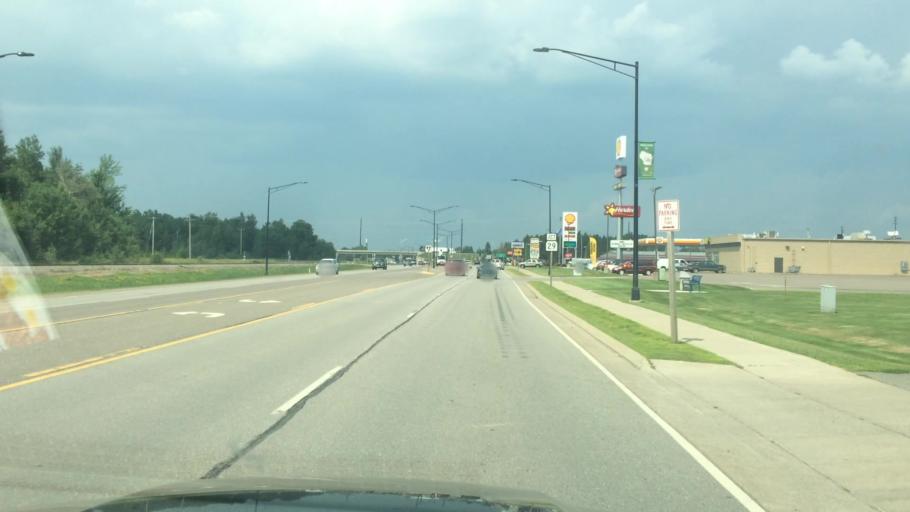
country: US
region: Wisconsin
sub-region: Clark County
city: Colby
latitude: 44.9272
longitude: -90.3154
